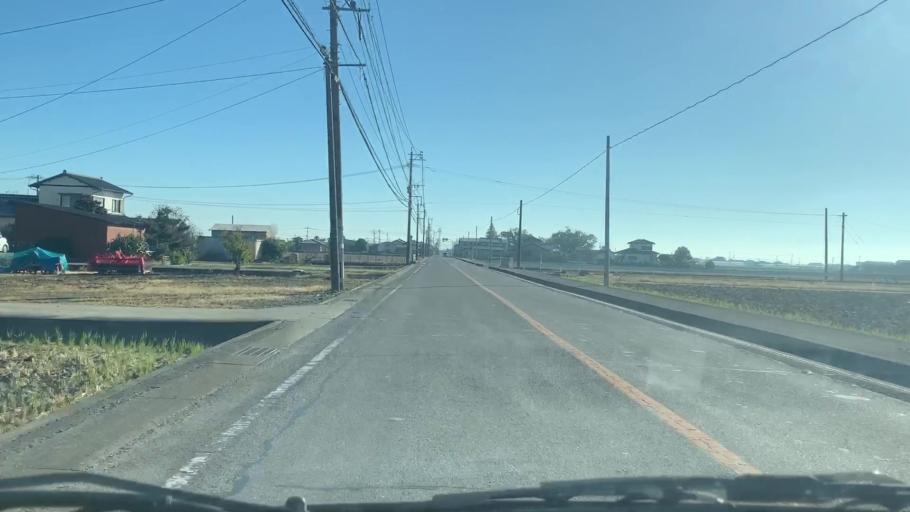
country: JP
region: Saga Prefecture
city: Kashima
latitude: 33.1839
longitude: 130.1678
